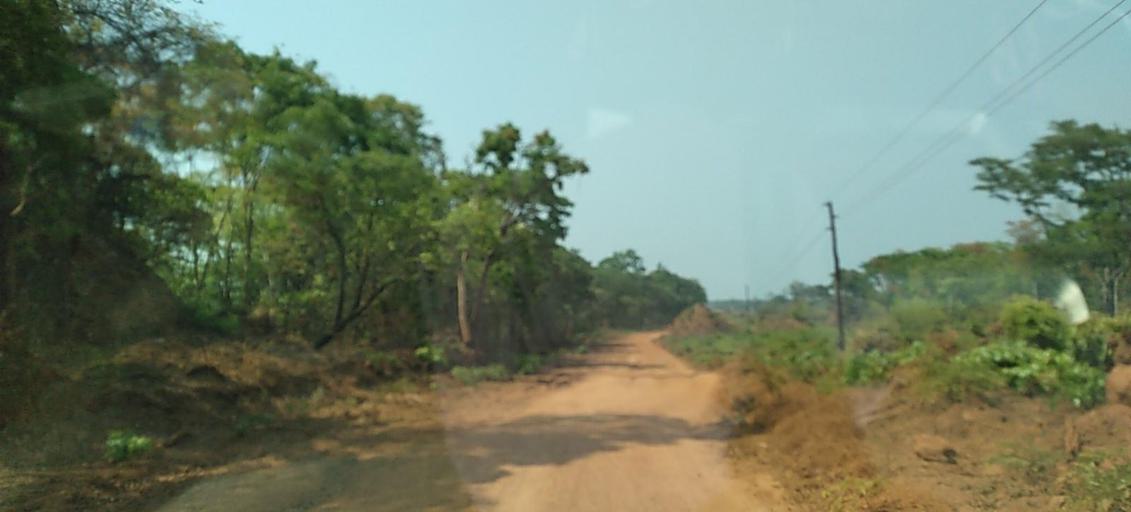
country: ZM
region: Copperbelt
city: Kalulushi
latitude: -13.0840
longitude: 27.4100
